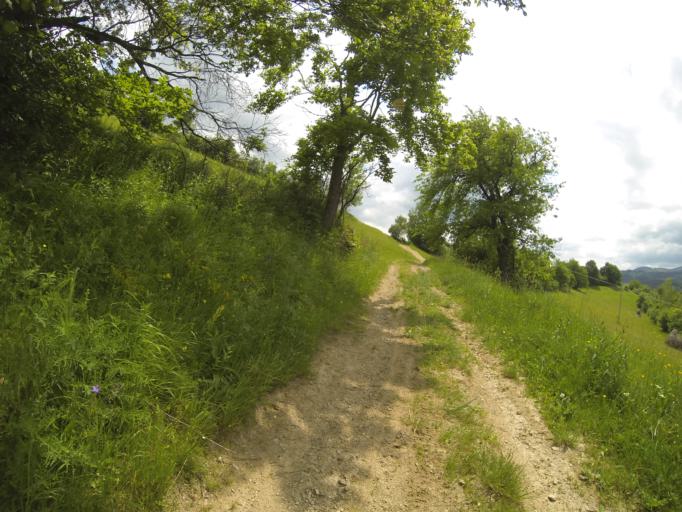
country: RO
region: Brasov
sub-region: Comuna Poiana Marului
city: Poiana Marului
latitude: 45.6464
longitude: 25.2842
